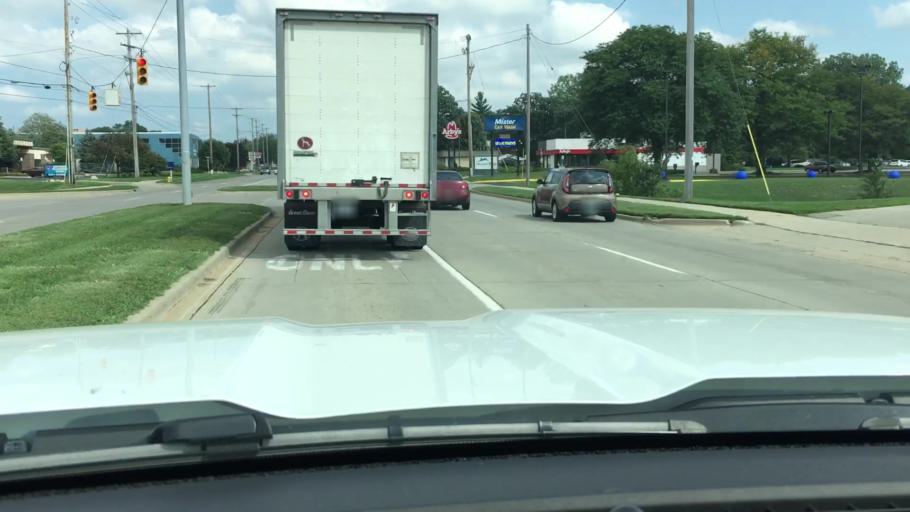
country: US
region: Michigan
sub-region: Kent County
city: Kentwood
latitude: 42.8839
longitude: -85.6512
